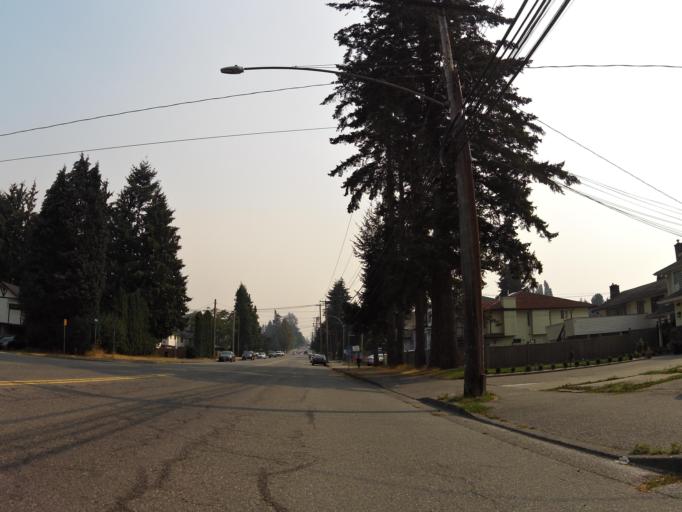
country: CA
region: British Columbia
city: Delta
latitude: 49.1560
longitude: -122.9174
